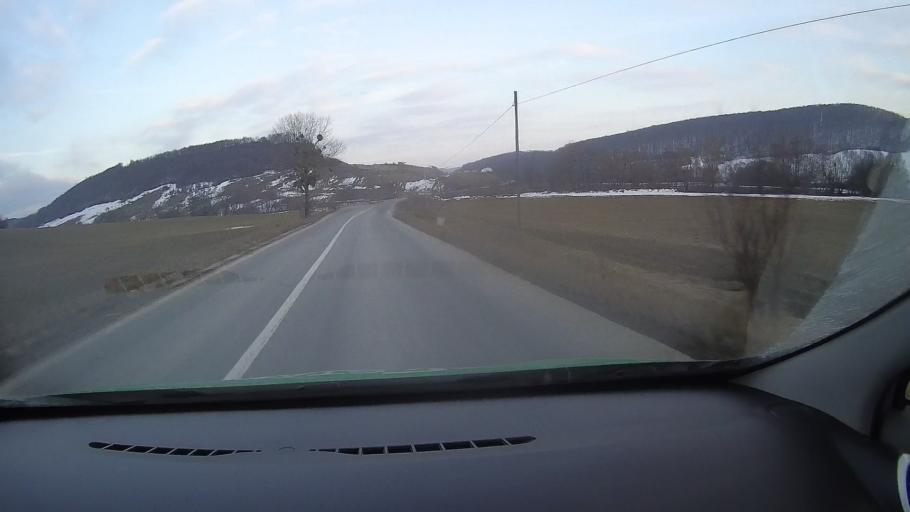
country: RO
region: Harghita
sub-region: Comuna Lupeni
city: Lupeni
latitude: 46.3608
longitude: 25.1859
